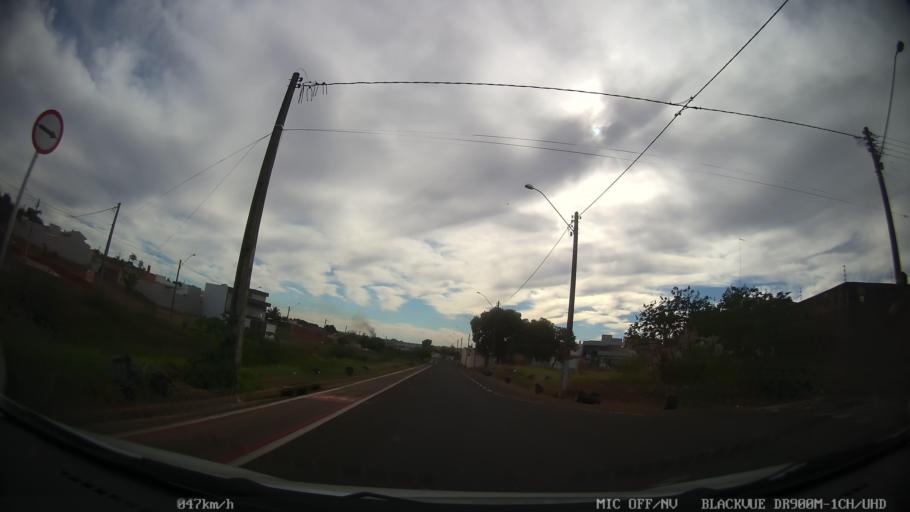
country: BR
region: Sao Paulo
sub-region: Catanduva
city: Catanduva
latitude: -21.1455
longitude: -48.9912
